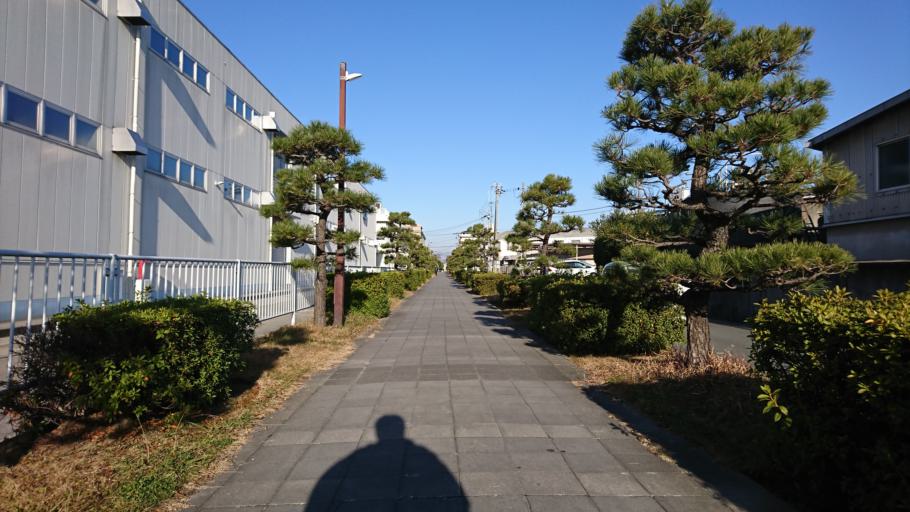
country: JP
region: Hyogo
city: Kakogawacho-honmachi
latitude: 34.7476
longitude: 134.8406
